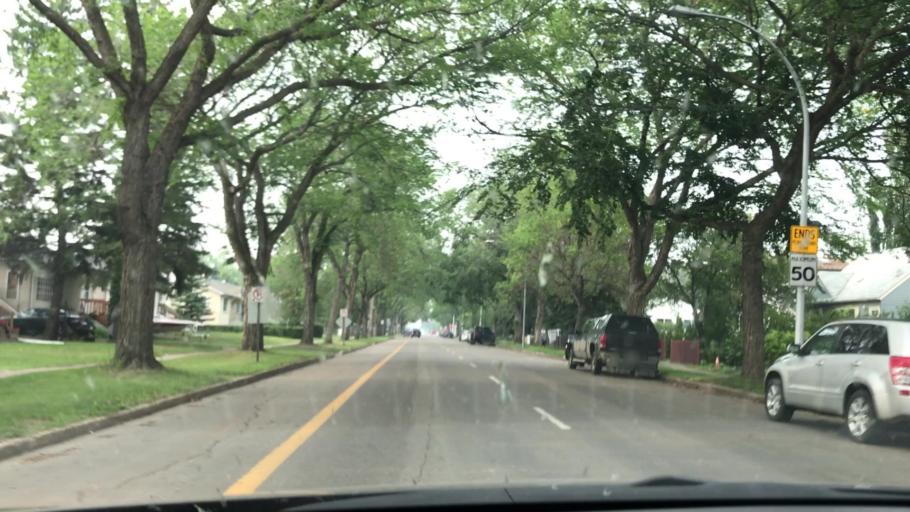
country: CA
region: Alberta
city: Edmonton
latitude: 53.5669
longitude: -113.5412
